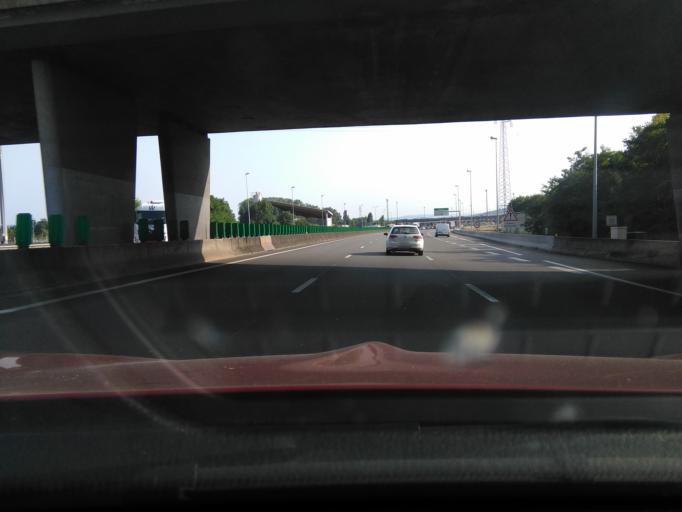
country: FR
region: Rhone-Alpes
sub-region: Departement du Rhone
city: Villefranche-sur-Saone
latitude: 45.9787
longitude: 4.7360
